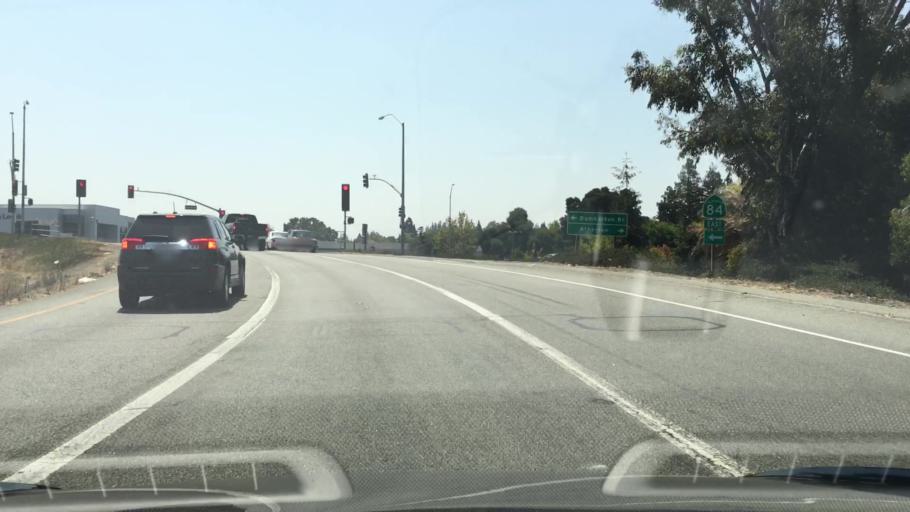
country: US
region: California
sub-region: San Mateo County
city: North Fair Oaks
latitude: 37.4832
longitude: -122.1823
